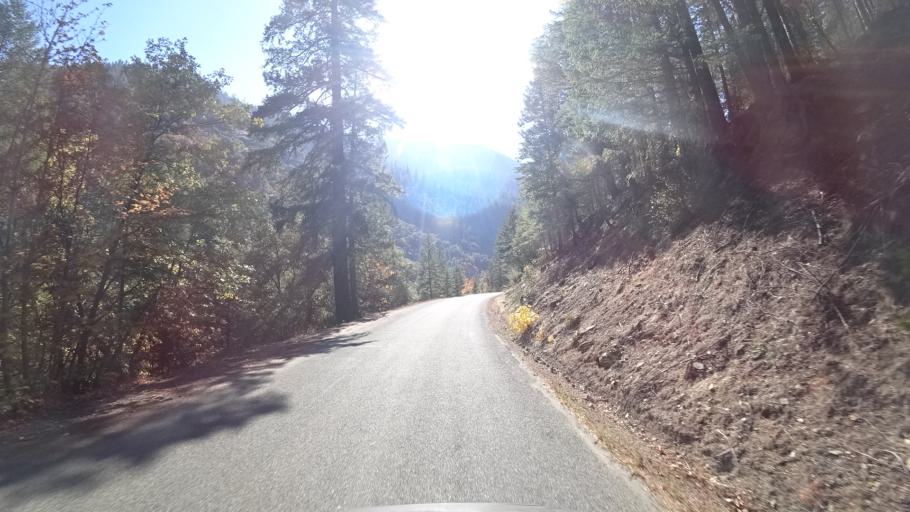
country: US
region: California
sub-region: Siskiyou County
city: Happy Camp
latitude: 41.6772
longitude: -123.1025
